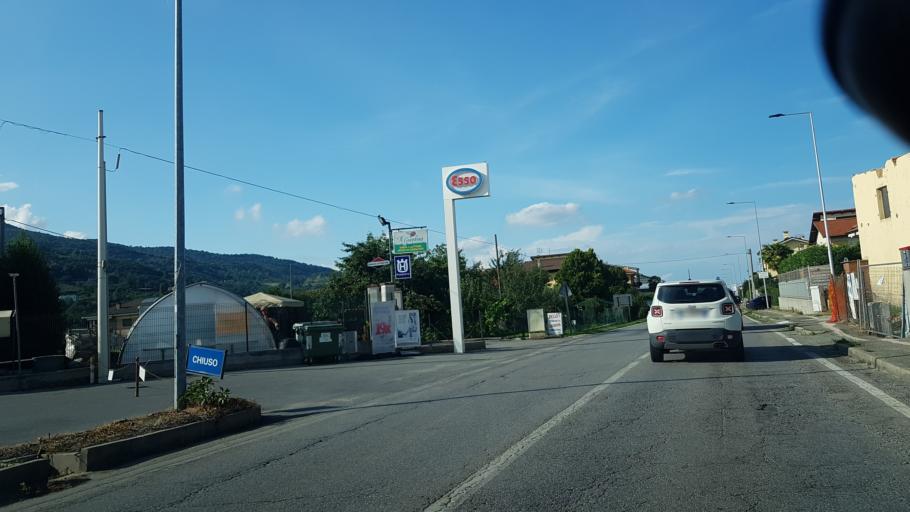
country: IT
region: Piedmont
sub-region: Provincia di Cuneo
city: Busca
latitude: 44.5224
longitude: 7.4793
